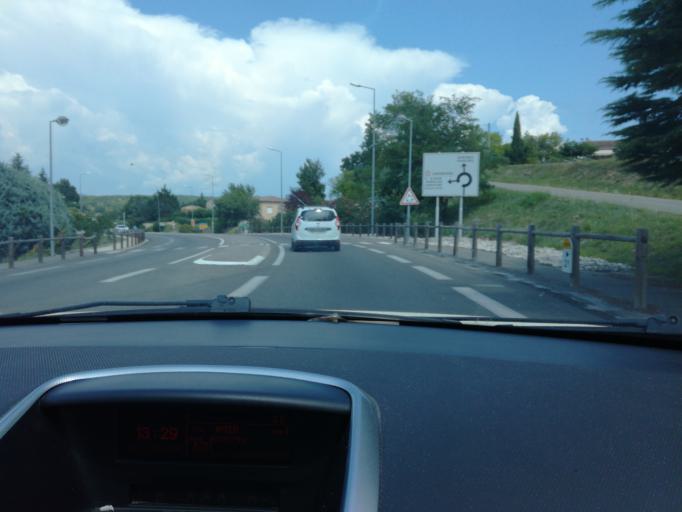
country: FR
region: Rhone-Alpes
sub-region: Departement de l'Ardeche
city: Ruoms
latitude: 44.4574
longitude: 4.3438
